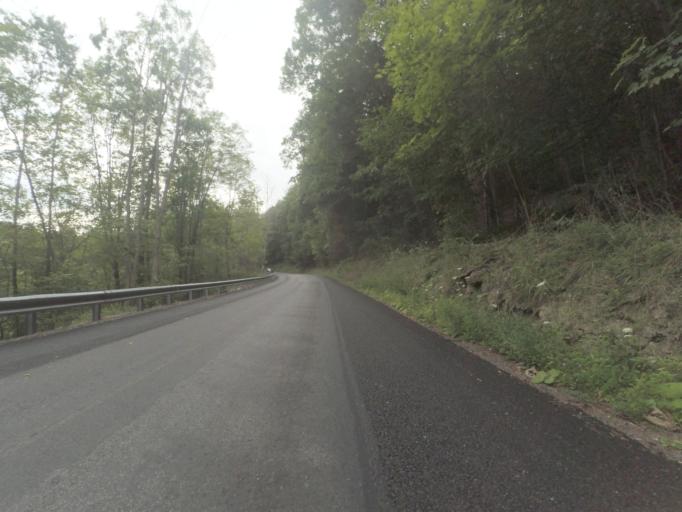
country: US
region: Pennsylvania
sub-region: Centre County
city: Zion
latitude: 41.0472
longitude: -77.6899
